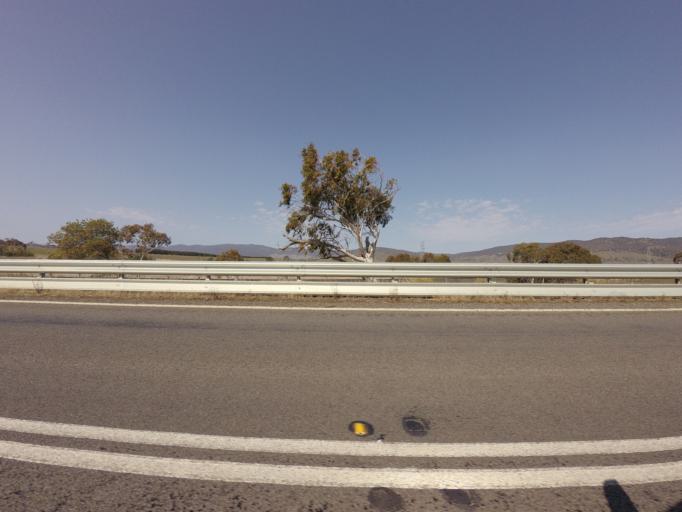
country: AU
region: Tasmania
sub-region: Northern Midlands
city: Evandale
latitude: -41.7985
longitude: 147.7006
